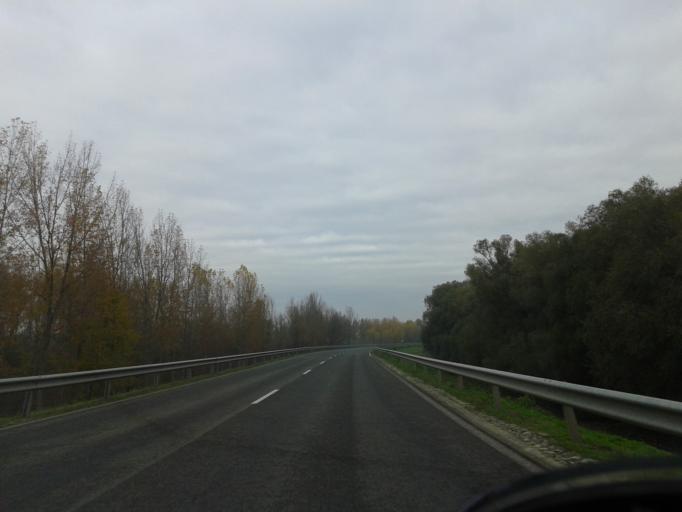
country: HU
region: Fejer
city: Adony
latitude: 47.1440
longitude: 18.8600
